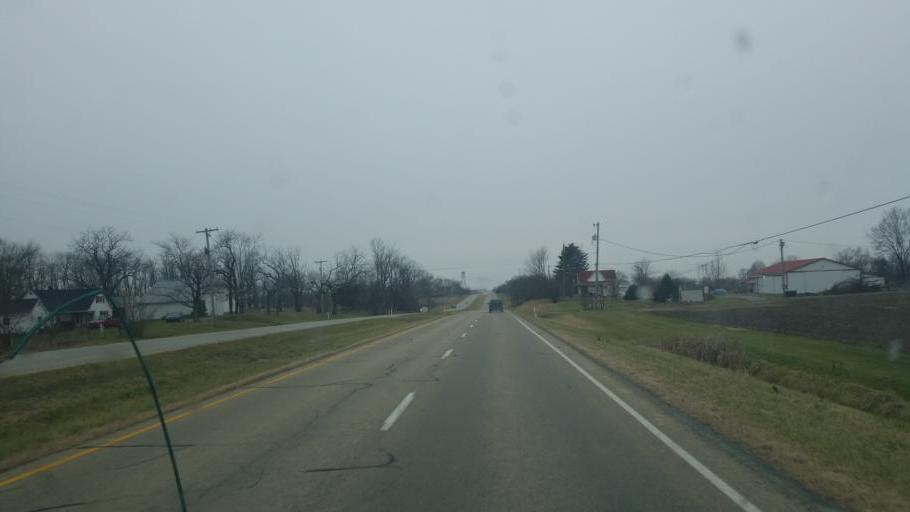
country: US
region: Indiana
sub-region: Hancock County
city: Greenfield
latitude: 39.7903
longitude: -85.6510
